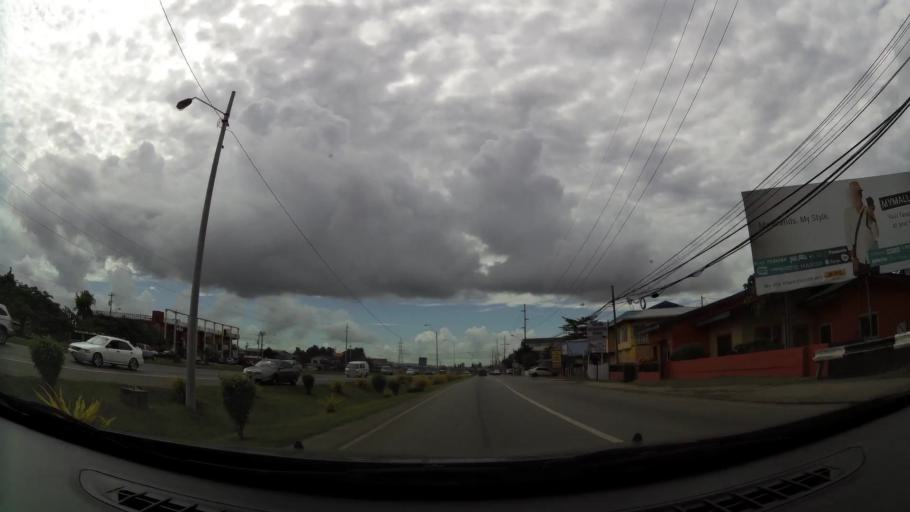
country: TT
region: Chaguanas
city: Chaguanas
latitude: 10.5099
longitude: -61.4075
